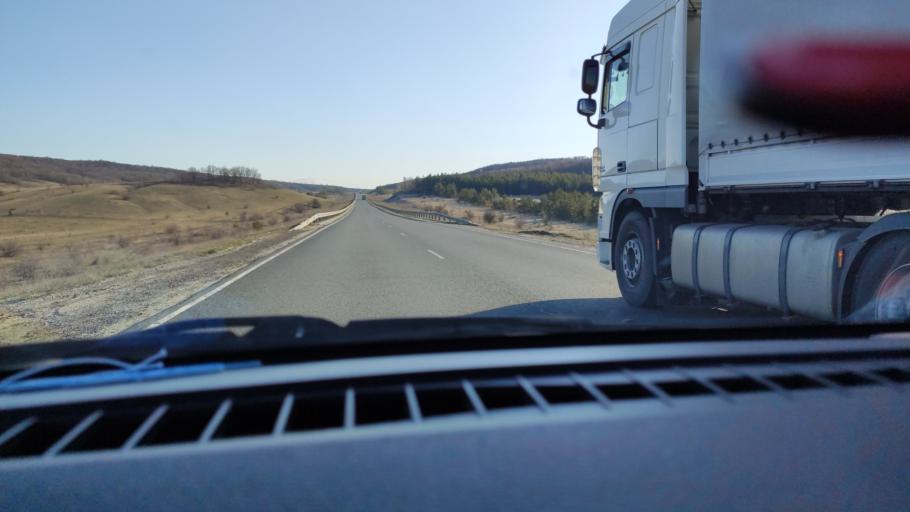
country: RU
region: Saratov
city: Alekseyevka
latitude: 52.3996
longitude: 47.9880
